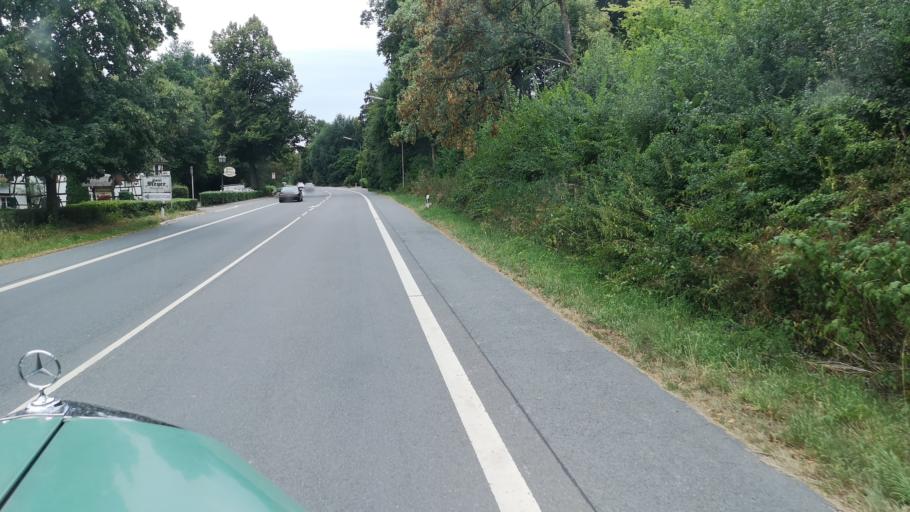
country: DE
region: North Rhine-Westphalia
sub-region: Regierungsbezirk Koln
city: Kurten
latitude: 51.0514
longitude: 7.2322
